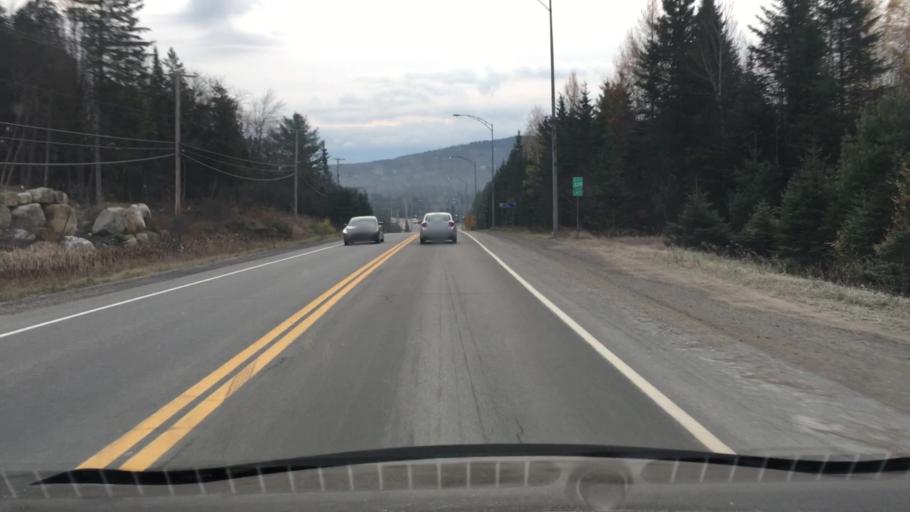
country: CA
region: Quebec
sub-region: Laurentides
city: Saint-Sauveur
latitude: 45.9061
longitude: -74.2507
